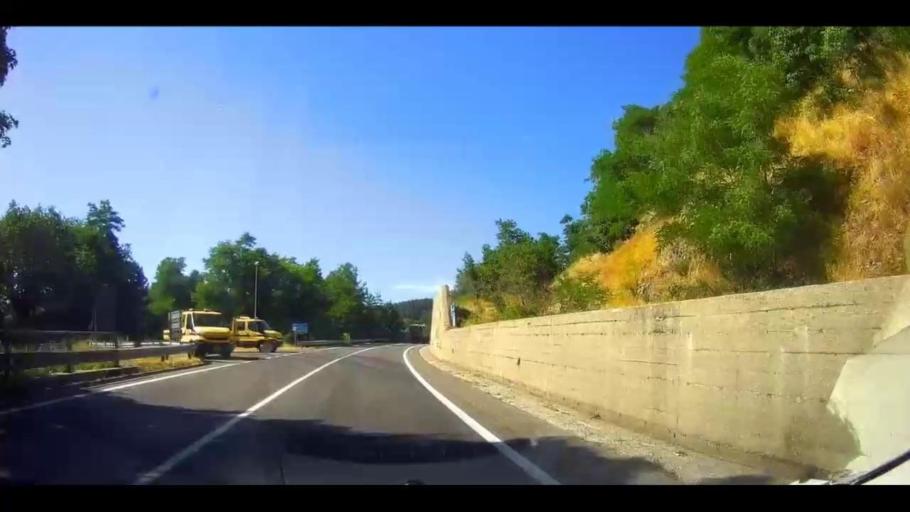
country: IT
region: Calabria
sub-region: Provincia di Cosenza
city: Celico
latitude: 39.3308
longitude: 16.3617
